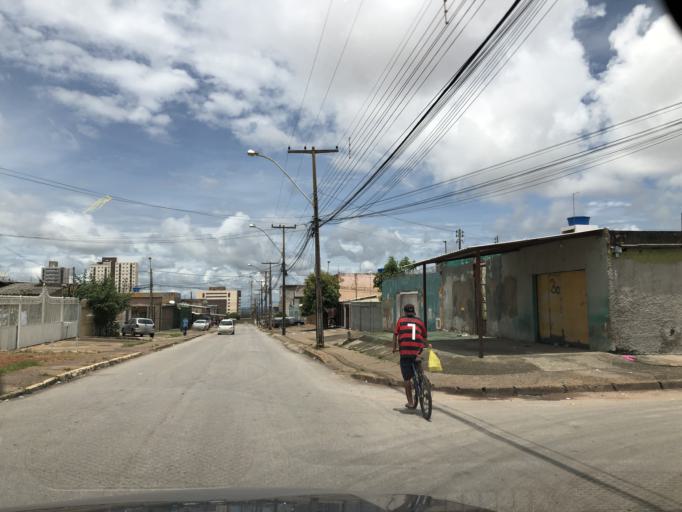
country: BR
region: Federal District
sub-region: Brasilia
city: Brasilia
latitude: -15.8146
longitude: -48.1118
